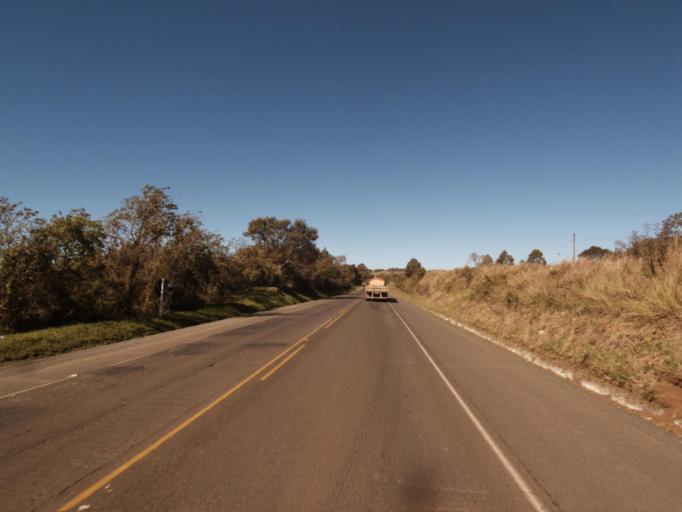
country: BR
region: Santa Catarina
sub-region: Chapeco
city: Chapeco
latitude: -26.9662
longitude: -52.7569
